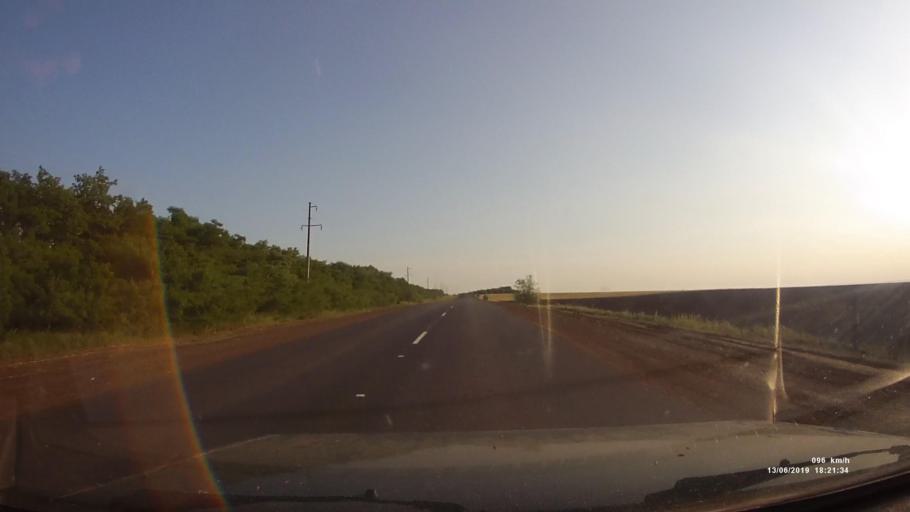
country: RU
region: Rostov
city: Kazanskaya
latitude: 49.8690
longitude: 41.2897
